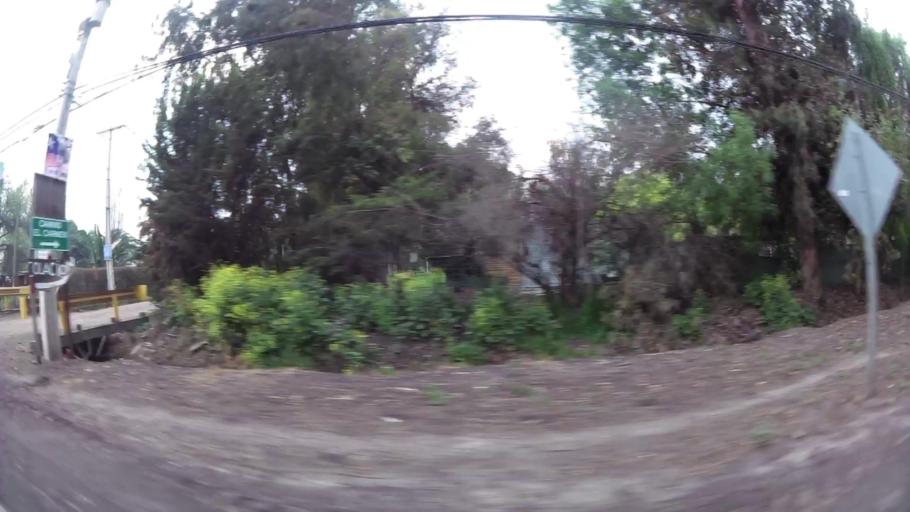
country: CL
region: Santiago Metropolitan
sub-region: Provincia de Chacabuco
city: Chicureo Abajo
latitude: -33.2555
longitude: -70.7628
